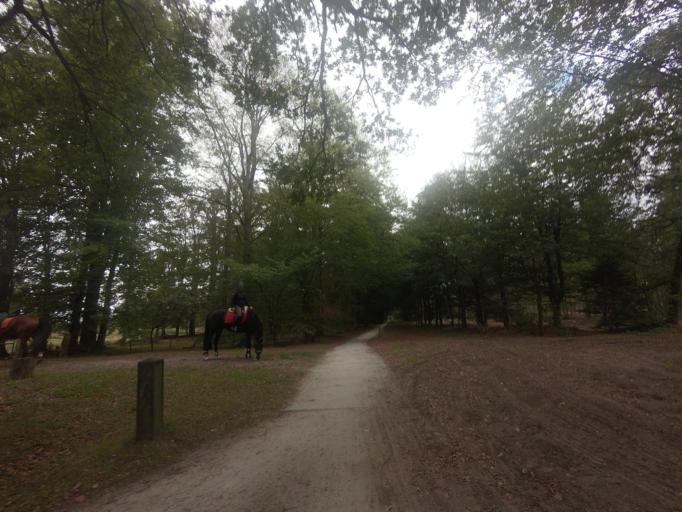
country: NL
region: Drenthe
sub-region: Gemeente Westerveld
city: Dwingeloo
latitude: 52.9272
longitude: 6.3199
